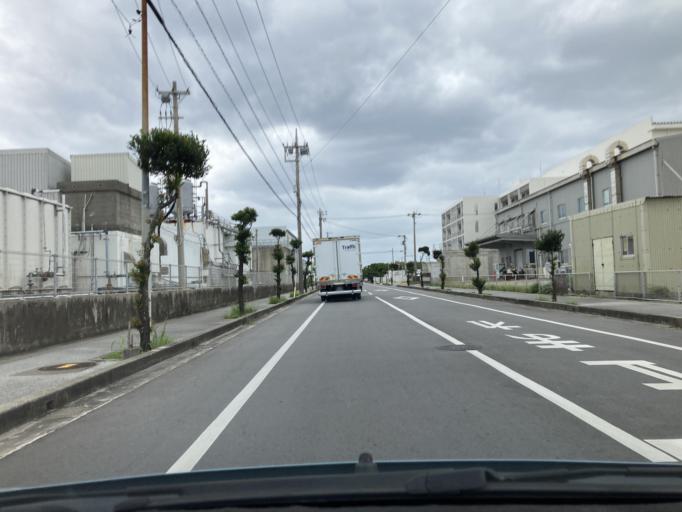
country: JP
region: Okinawa
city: Itoman
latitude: 26.1383
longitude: 127.6562
